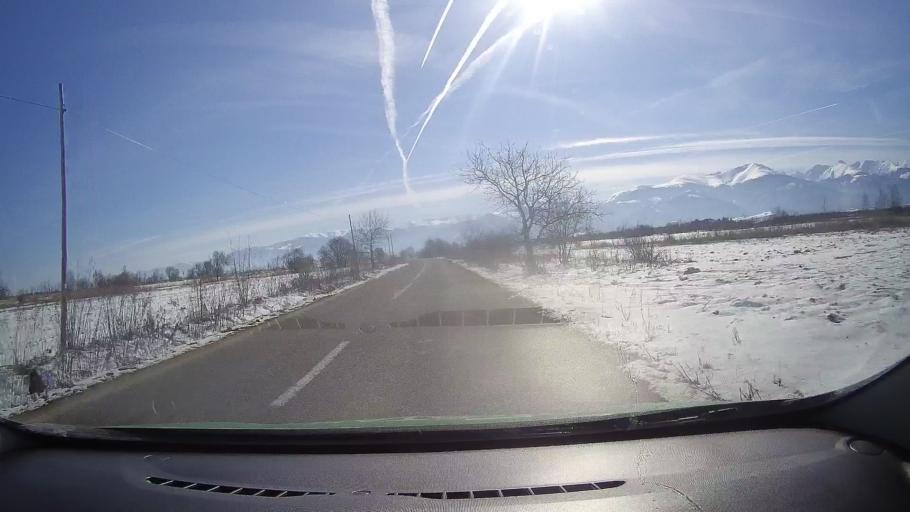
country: RO
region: Brasov
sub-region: Comuna Sambata de Sus
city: Sambata de Sus
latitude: 45.7486
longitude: 24.8386
